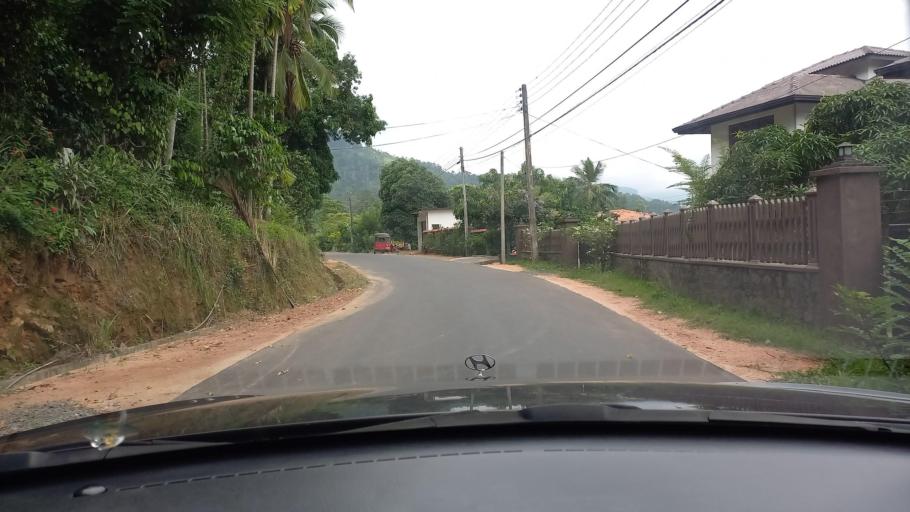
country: LK
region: Central
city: Gampola
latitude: 7.2045
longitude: 80.6259
